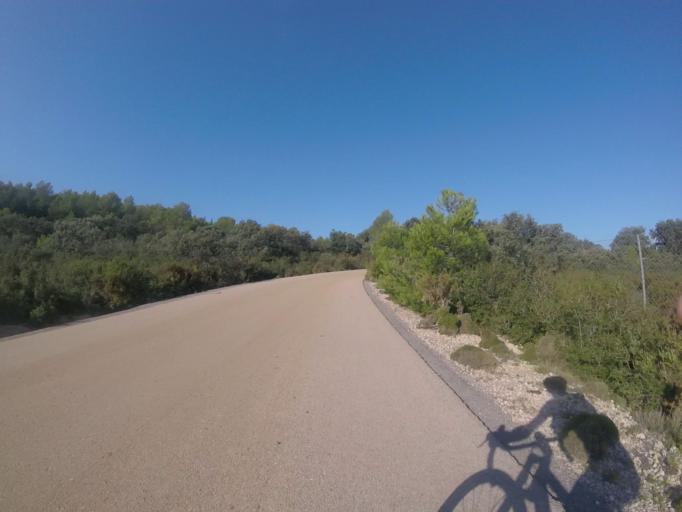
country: ES
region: Valencia
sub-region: Provincia de Castello
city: Benlloch
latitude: 40.2013
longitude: 0.0669
